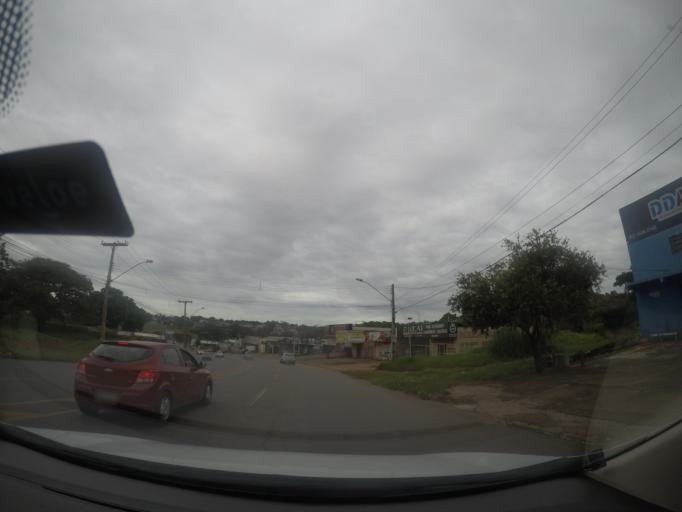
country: BR
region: Goias
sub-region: Goiania
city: Goiania
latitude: -16.6303
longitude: -49.2854
